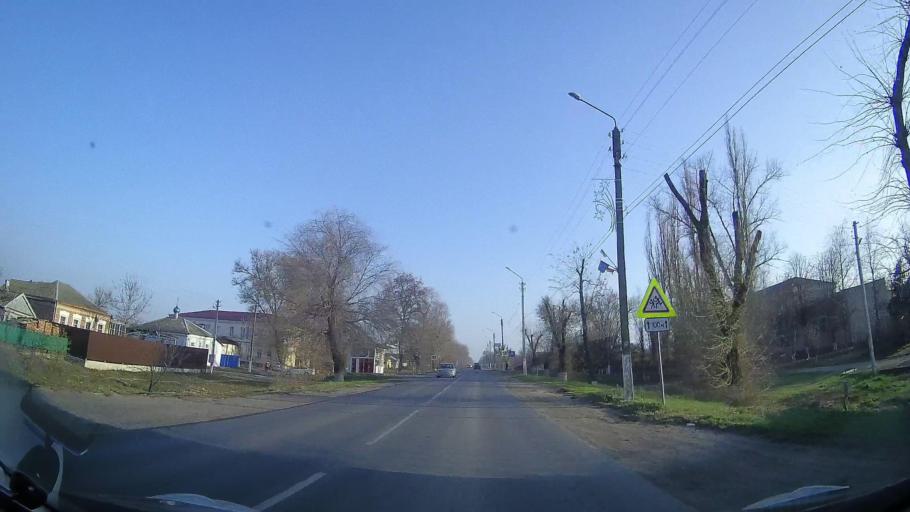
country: RU
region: Rostov
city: Ol'ginskaya
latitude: 47.1940
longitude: 39.9426
